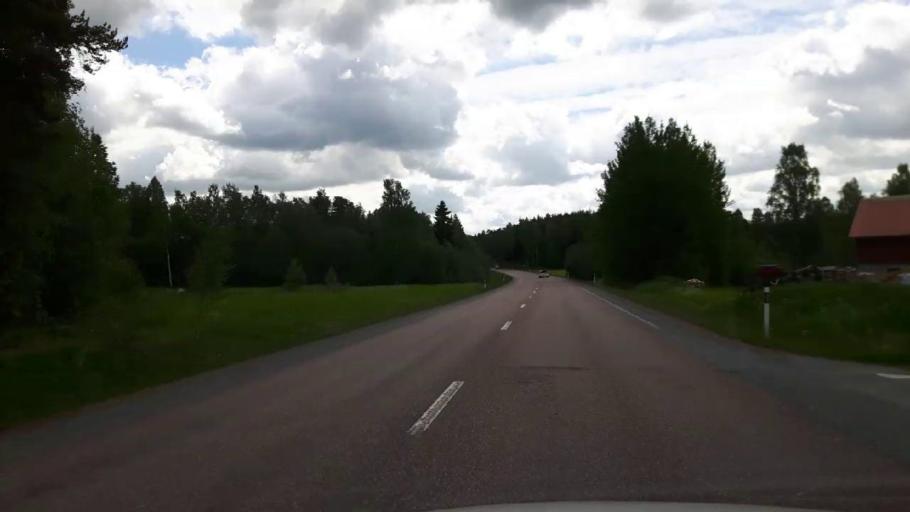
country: SE
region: Dalarna
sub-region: Faluns Kommun
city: Falun
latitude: 60.5102
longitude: 15.7371
